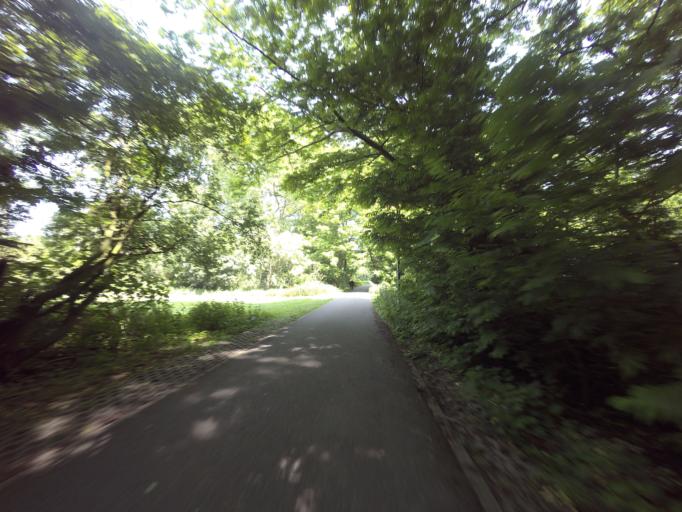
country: NL
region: North Holland
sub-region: Gemeente Amstelveen
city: Amstelveen
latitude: 52.3237
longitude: 4.8538
